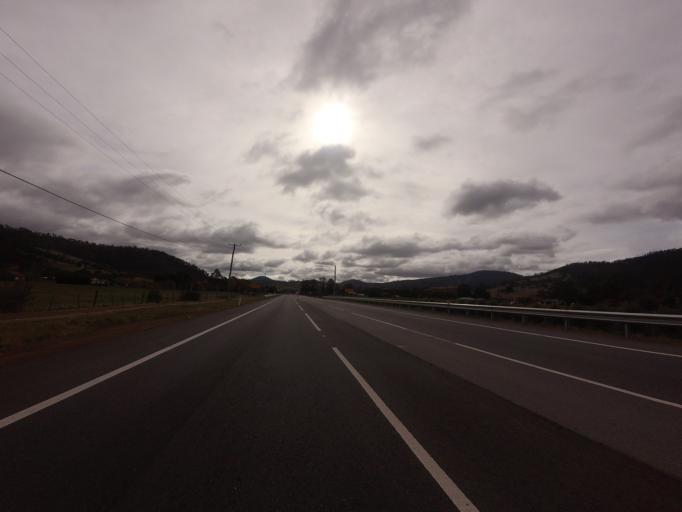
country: AU
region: Tasmania
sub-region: Brighton
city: Bridgewater
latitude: -42.6119
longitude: 147.2226
